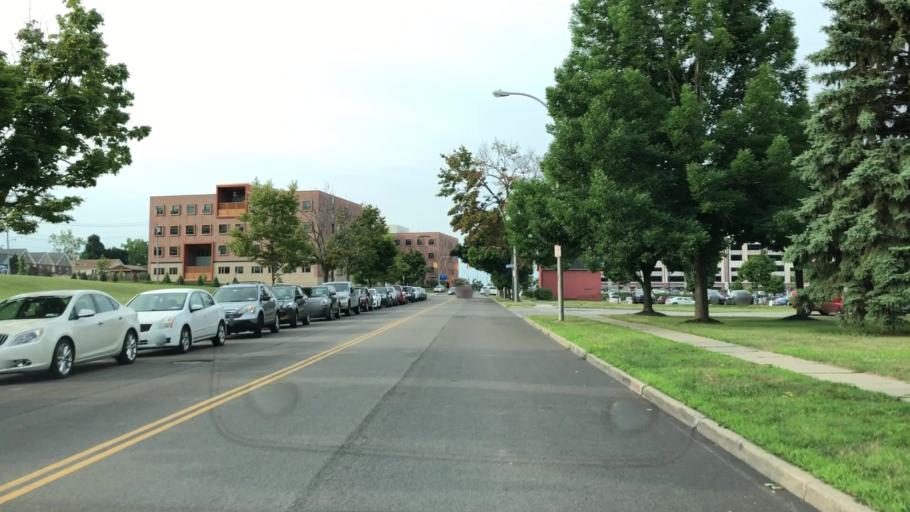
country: US
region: New York
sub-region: Erie County
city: Buffalo
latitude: 42.9035
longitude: -78.8627
